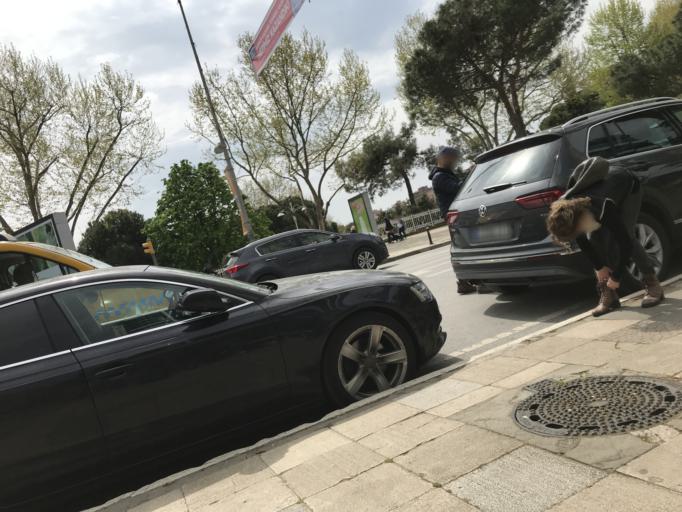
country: TR
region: Istanbul
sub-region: Atasehir
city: Atasehir
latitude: 40.9713
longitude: 29.0605
